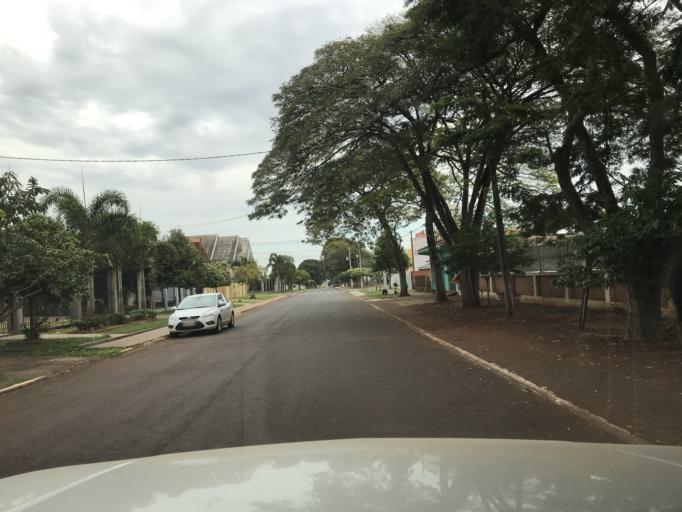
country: BR
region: Parana
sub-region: Marechal Candido Rondon
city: Marechal Candido Rondon
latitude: -24.4658
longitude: -53.9561
